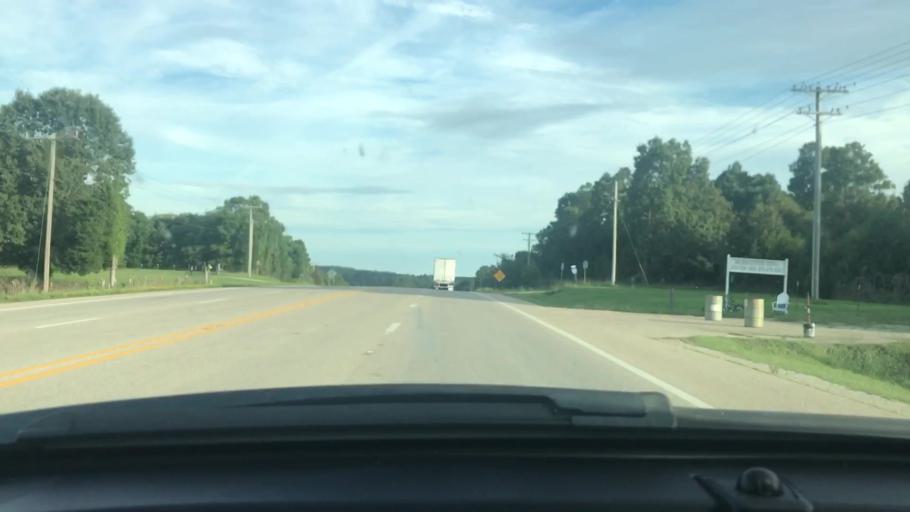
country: US
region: Arkansas
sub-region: Lawrence County
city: Hoxie
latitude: 36.1278
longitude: -91.1569
